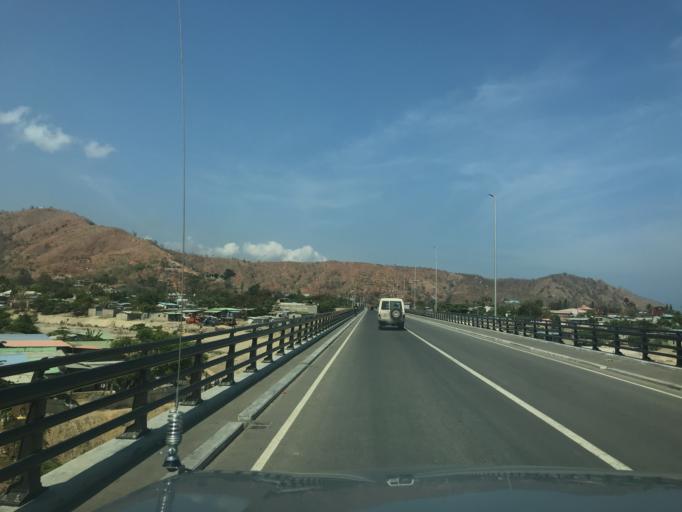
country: TL
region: Dili
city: Dili
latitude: -8.5610
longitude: 125.5351
